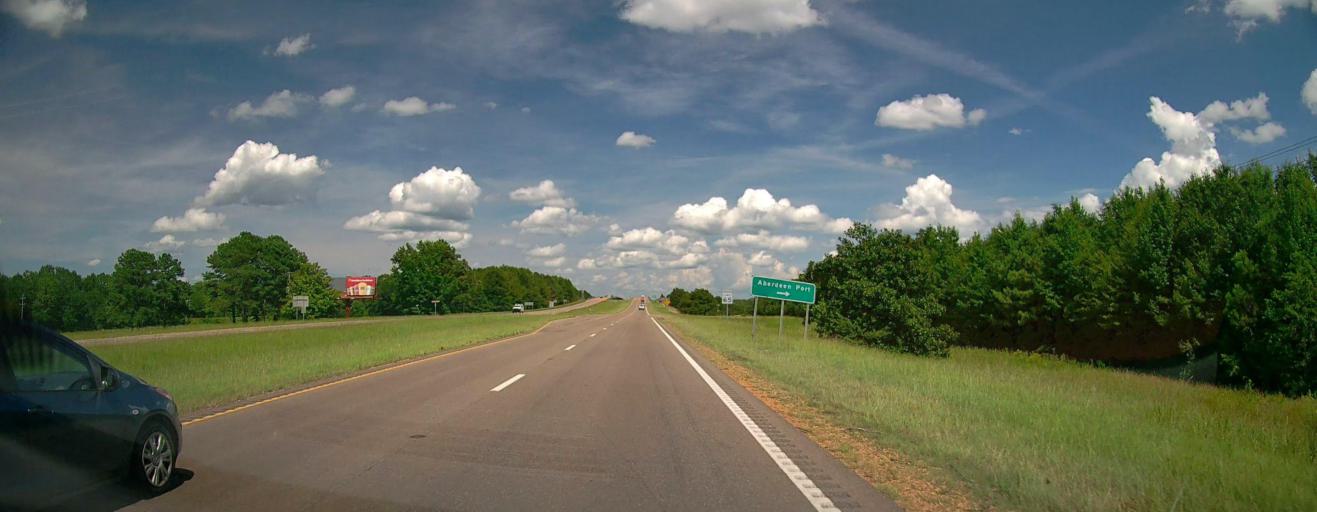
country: US
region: Mississippi
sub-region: Monroe County
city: Aberdeen
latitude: 33.8164
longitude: -88.5266
